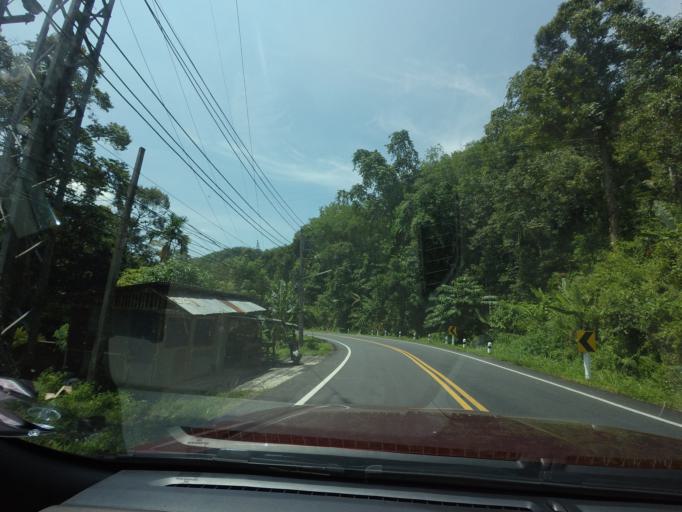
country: TH
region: Yala
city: Betong
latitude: 5.9119
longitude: 101.1552
